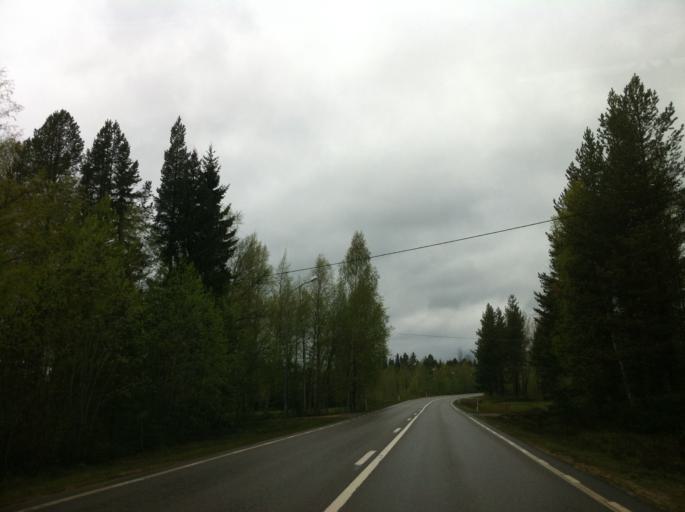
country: SE
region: Jaemtland
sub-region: Harjedalens Kommun
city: Sveg
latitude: 62.0623
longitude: 14.2812
